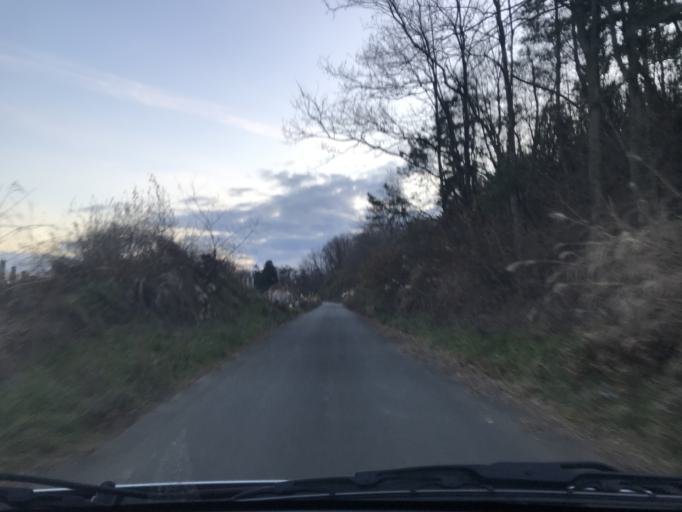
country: JP
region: Iwate
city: Ichinoseki
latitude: 38.8320
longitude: 141.0944
